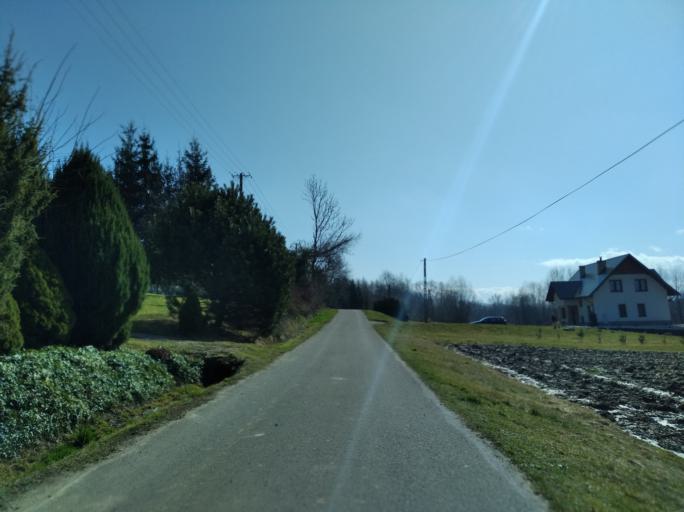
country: PL
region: Subcarpathian Voivodeship
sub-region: Powiat strzyzowski
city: Wysoka Strzyzowska
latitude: 49.8402
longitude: 21.7404
